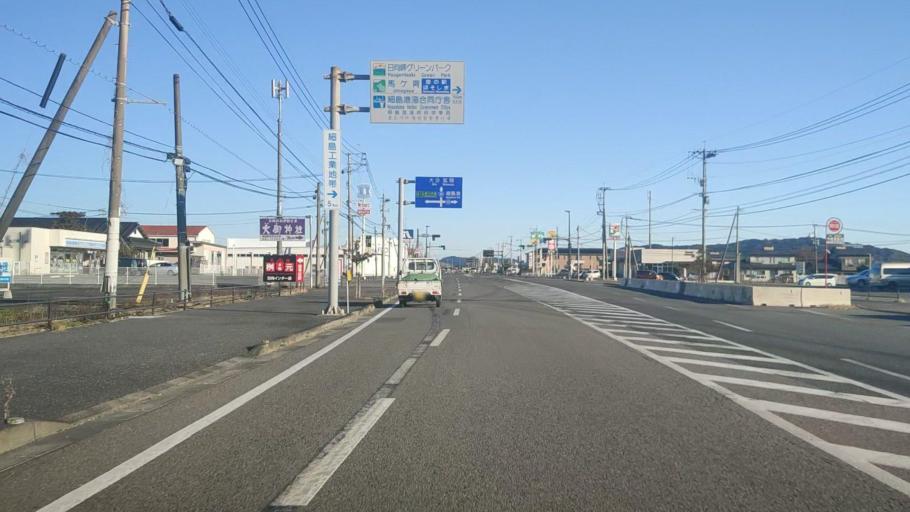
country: JP
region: Miyazaki
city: Nobeoka
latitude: 32.3957
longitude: 131.6291
